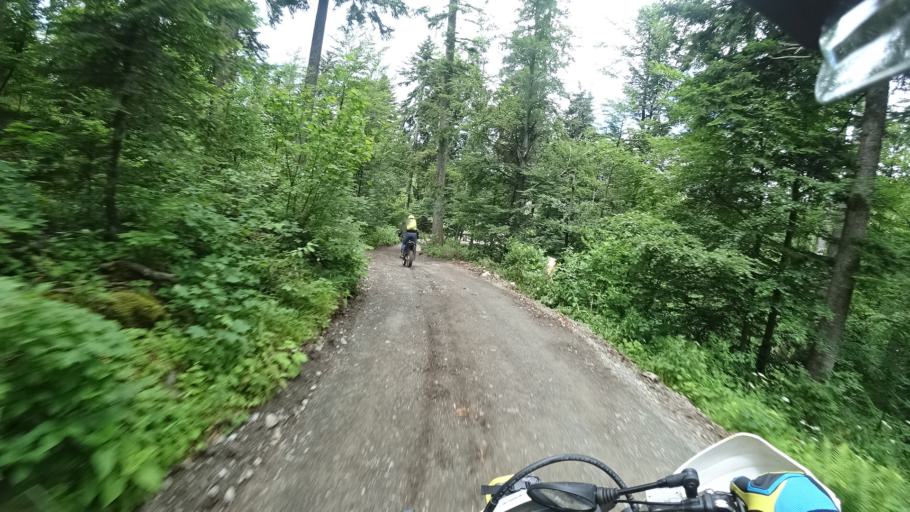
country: HR
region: Primorsko-Goranska
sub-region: Grad Delnice
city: Delnice
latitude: 45.3074
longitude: 14.7499
